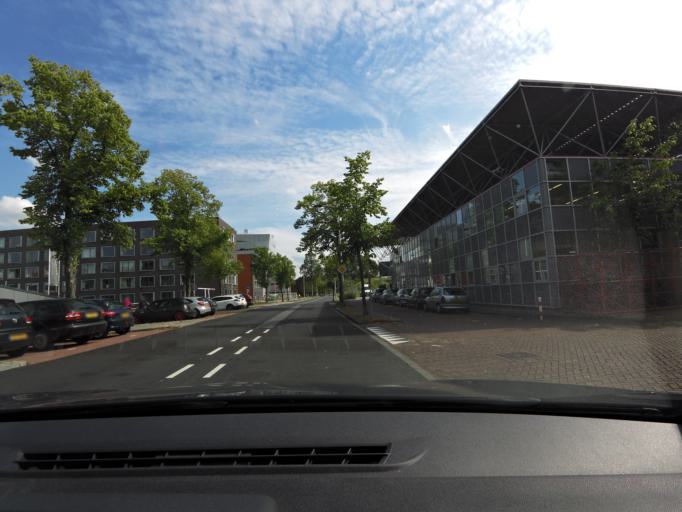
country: NL
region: South Holland
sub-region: Gemeente Delft
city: Delft
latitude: 52.0015
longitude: 4.3674
